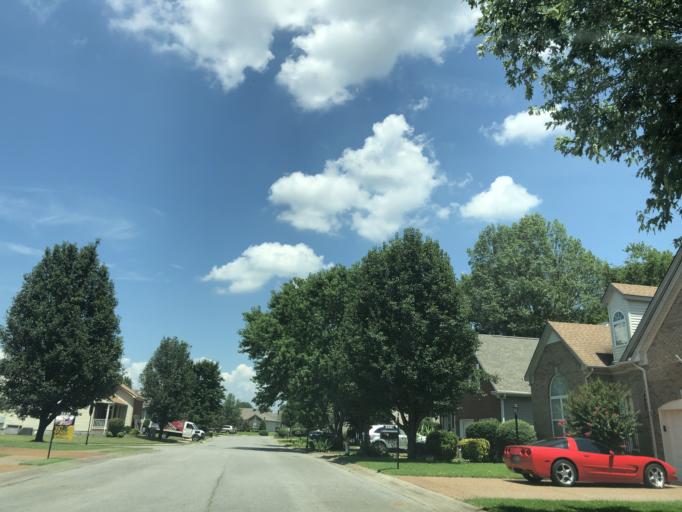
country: US
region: Tennessee
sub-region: Davidson County
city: Lakewood
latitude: 36.1773
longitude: -86.6402
